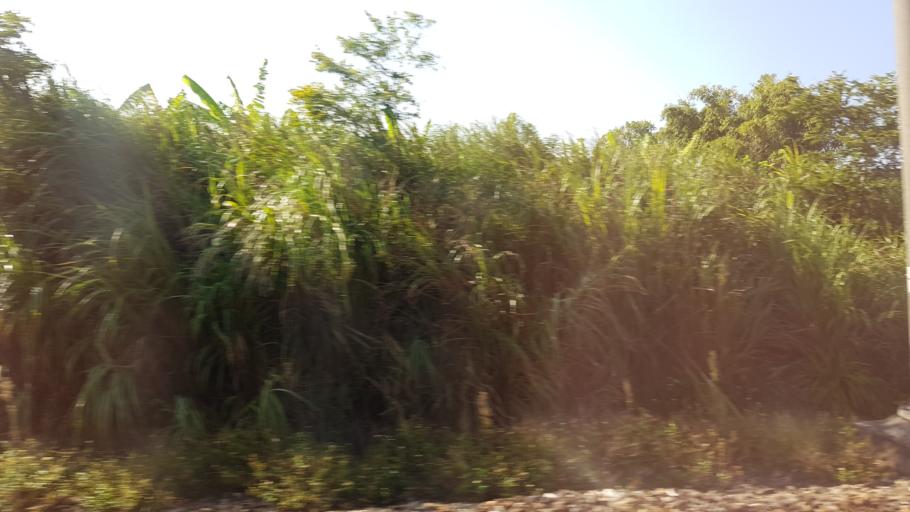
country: TW
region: Taiwan
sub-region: Miaoli
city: Miaoli
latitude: 24.6594
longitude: 120.8771
